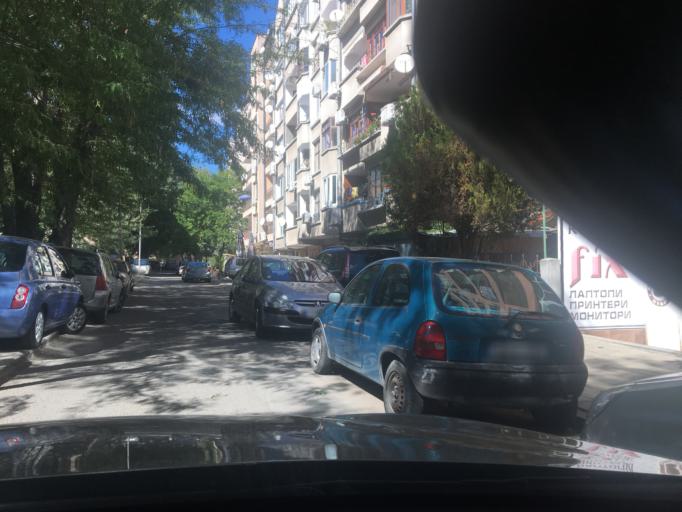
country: BG
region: Burgas
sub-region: Obshtina Burgas
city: Burgas
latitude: 42.5092
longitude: 27.4725
